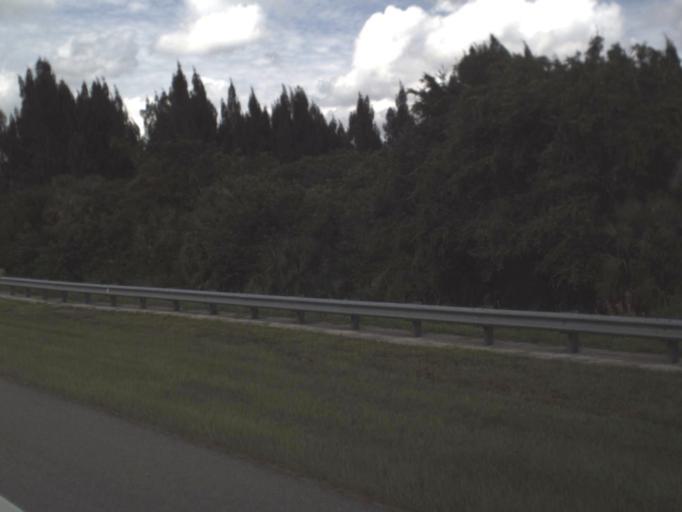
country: US
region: Florida
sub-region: Collier County
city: Immokalee
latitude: 26.4095
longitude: -81.3986
